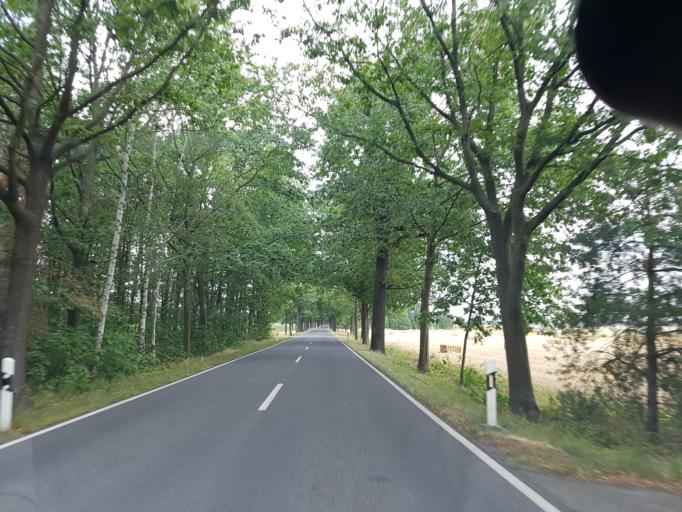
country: DE
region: Brandenburg
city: Sallgast
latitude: 51.5950
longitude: 13.8458
